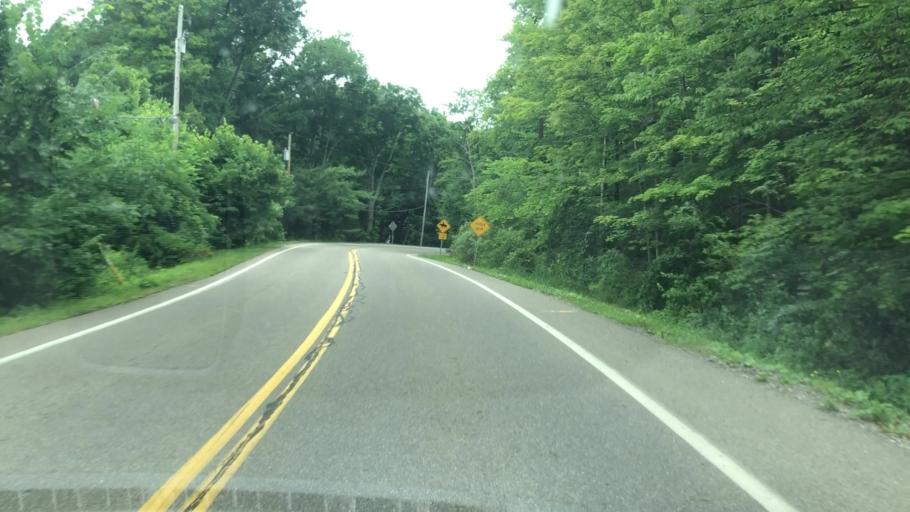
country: US
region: Ohio
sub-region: Summit County
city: Montrose-Ghent
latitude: 41.1571
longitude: -81.6346
